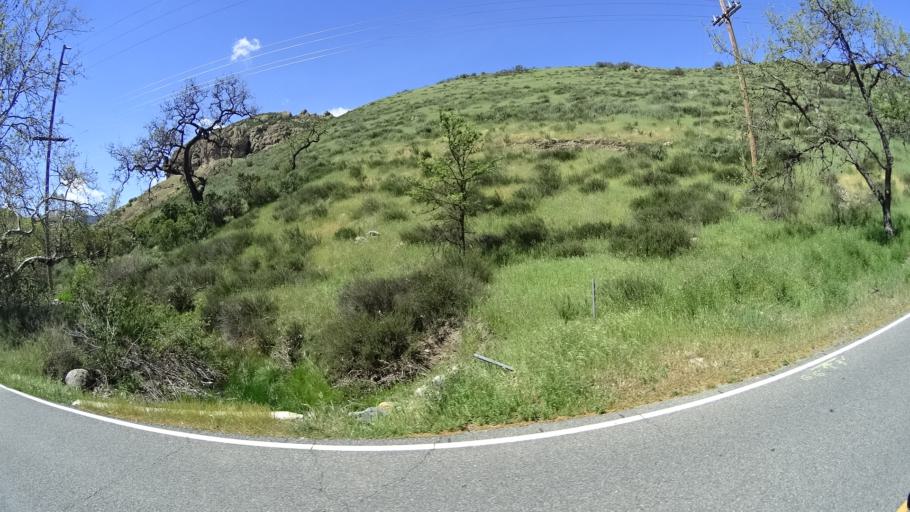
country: US
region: California
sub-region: Ventura County
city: Thousand Oaks
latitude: 34.1389
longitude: -118.8499
